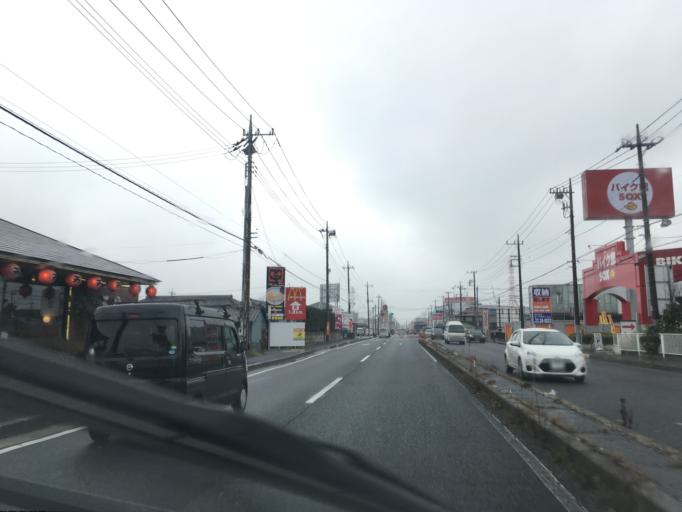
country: JP
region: Saitama
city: Koshigaya
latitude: 35.8847
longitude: 139.7736
